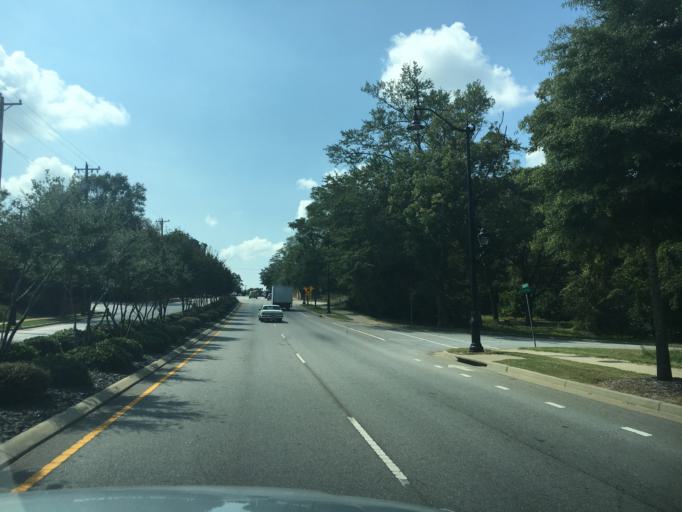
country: US
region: South Carolina
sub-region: Greenville County
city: Greenville
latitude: 34.8362
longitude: -82.4017
